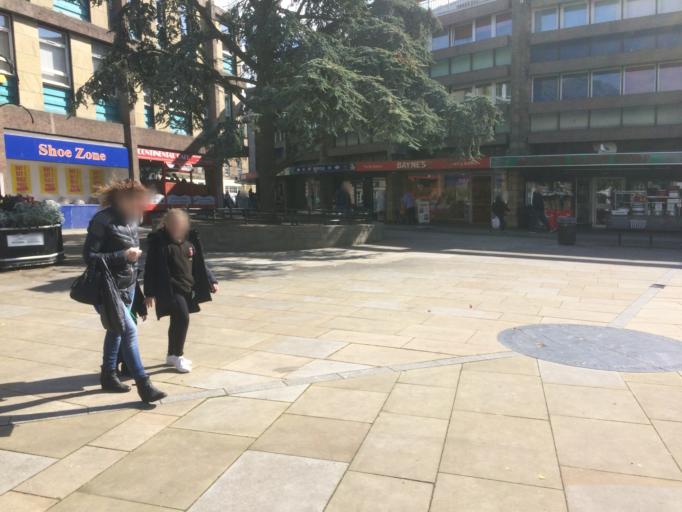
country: GB
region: Scotland
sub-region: Midlothian
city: Dalkeith
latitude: 55.8940
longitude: -3.0706
